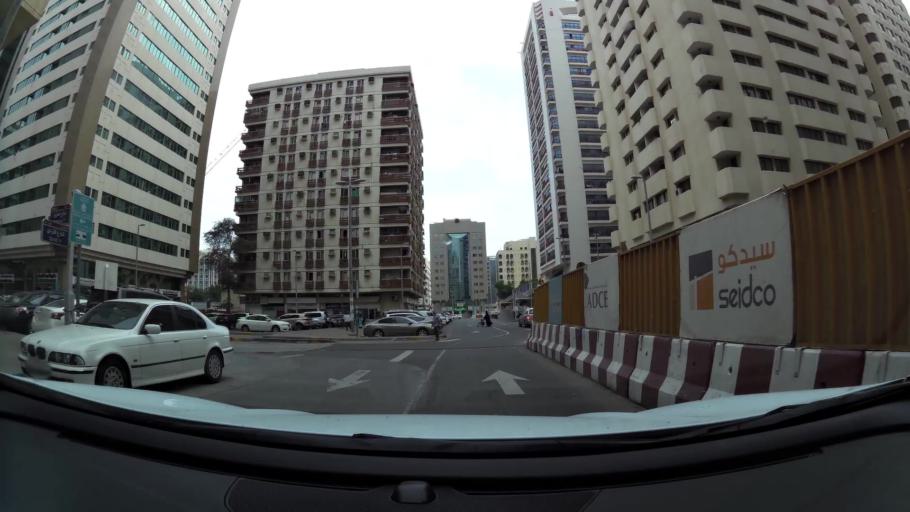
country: AE
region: Abu Dhabi
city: Abu Dhabi
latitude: 24.4949
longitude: 54.3792
